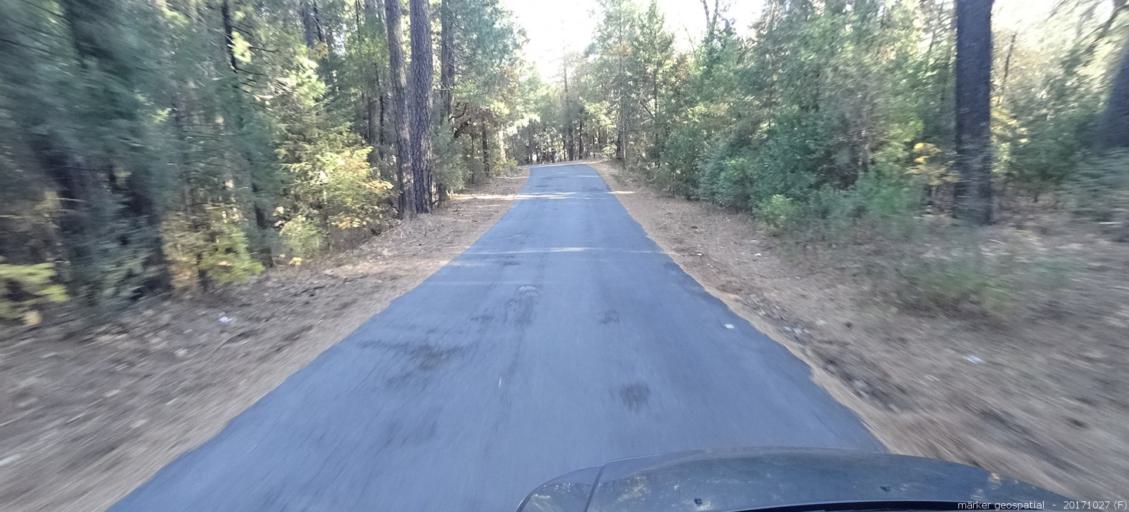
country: US
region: California
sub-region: Shasta County
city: Burney
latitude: 41.0096
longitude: -121.8969
